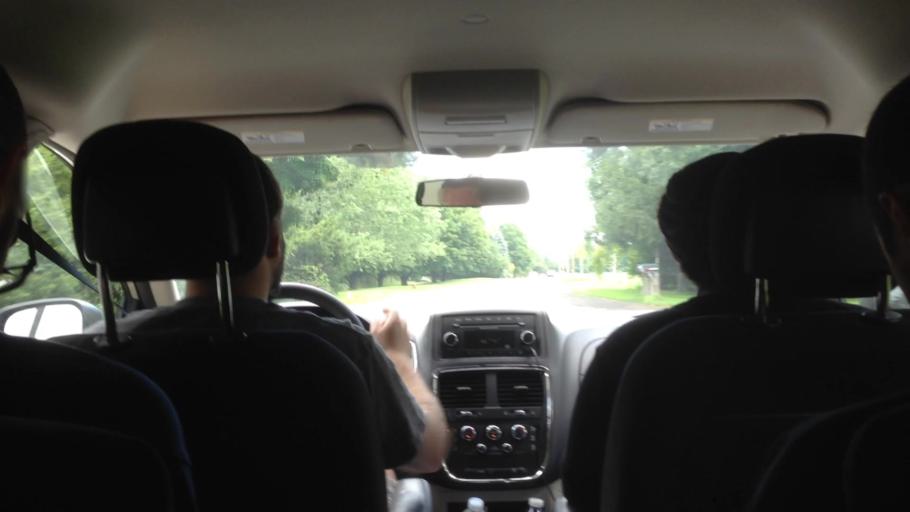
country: US
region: New York
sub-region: Dutchess County
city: Red Hook
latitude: 42.0004
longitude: -73.8717
